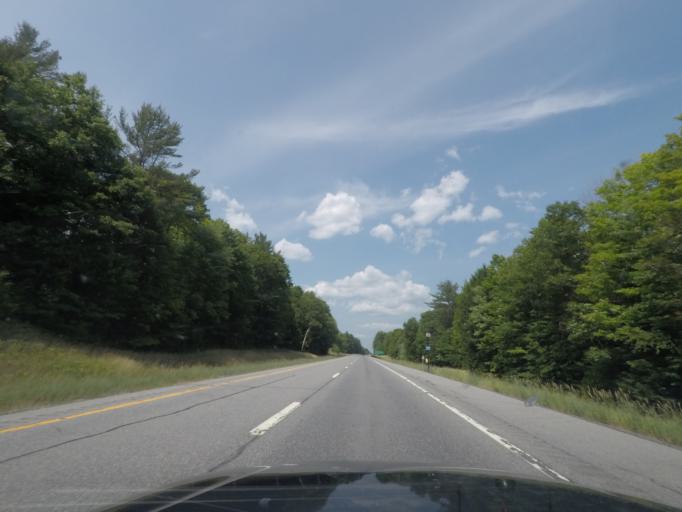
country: US
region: New York
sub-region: Essex County
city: Ticonderoga
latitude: 43.8477
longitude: -73.7661
